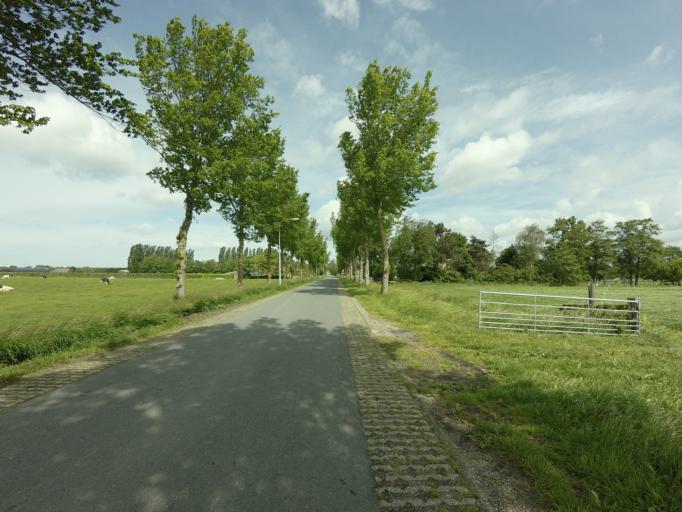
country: NL
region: North Holland
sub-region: Gemeente Hoorn
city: Hoorn
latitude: 52.6797
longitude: 5.0113
